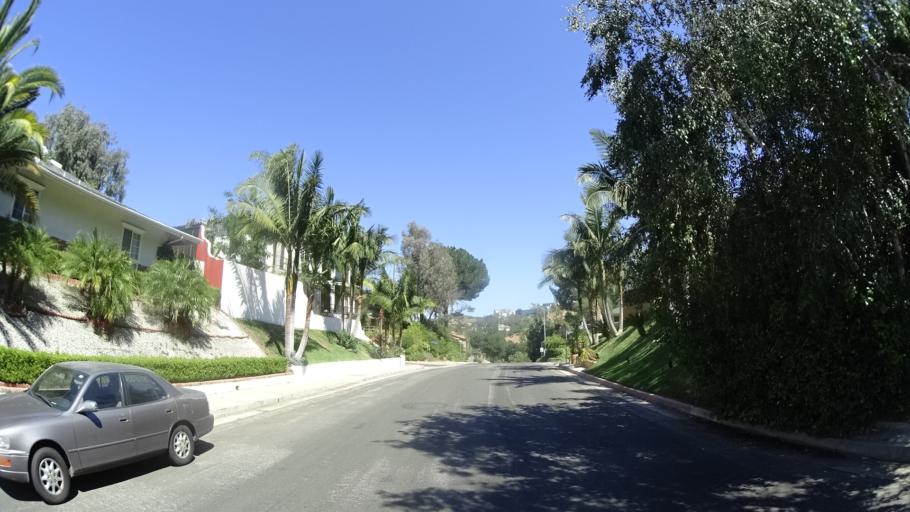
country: US
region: California
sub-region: Los Angeles County
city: Sherman Oaks
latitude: 34.1351
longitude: -118.4924
